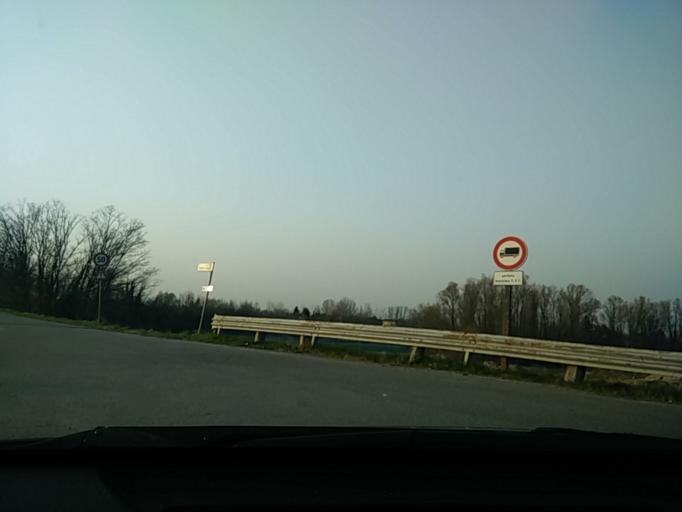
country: IT
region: Veneto
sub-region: Provincia di Venezia
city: Fossalta di Piave
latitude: 45.6501
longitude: 12.5147
